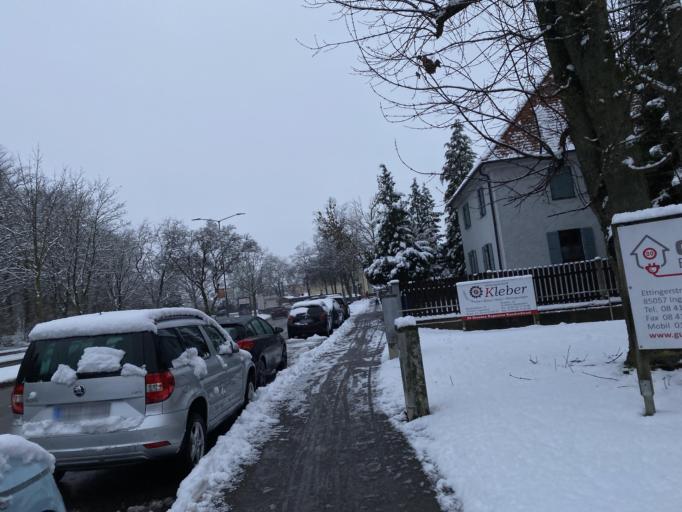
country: DE
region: Bavaria
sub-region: Upper Bavaria
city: Ingolstadt
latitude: 48.7717
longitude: 11.4170
